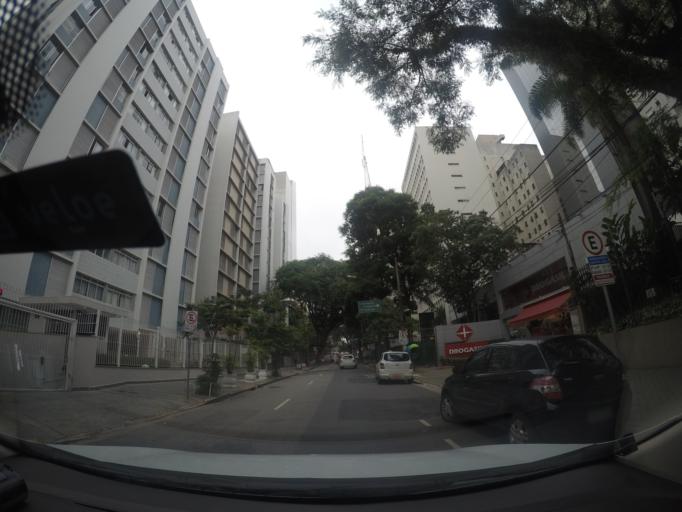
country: BR
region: Sao Paulo
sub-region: Sao Paulo
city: Sao Paulo
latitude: -23.5619
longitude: -46.6522
